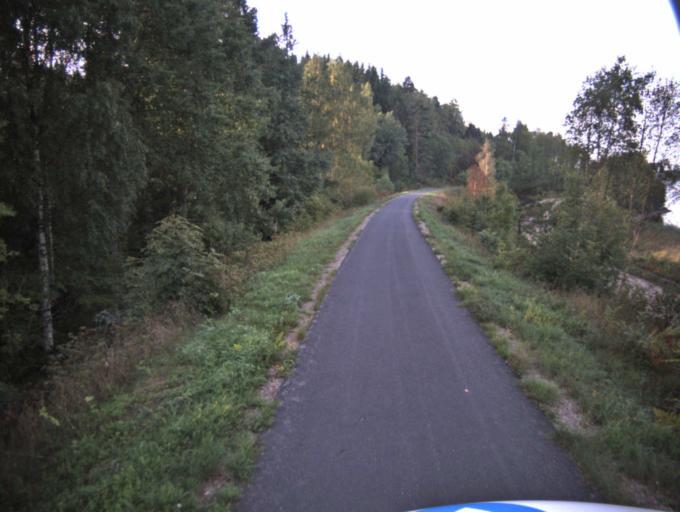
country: SE
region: Vaestra Goetaland
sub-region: Ulricehamns Kommun
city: Ulricehamn
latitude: 57.7581
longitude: 13.4000
